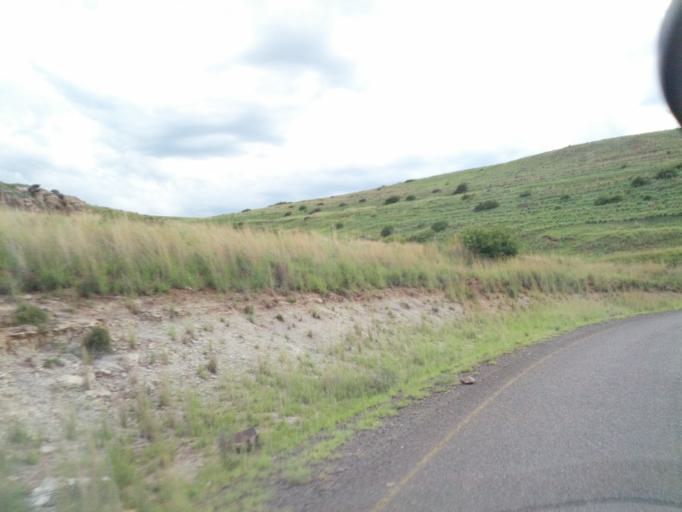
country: LS
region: Qacha's Nek
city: Qacha's Nek
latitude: -30.0535
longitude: 28.4989
